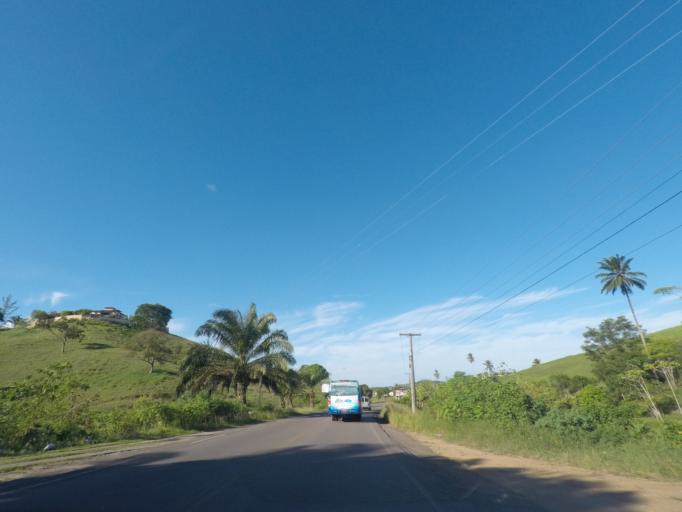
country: BR
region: Bahia
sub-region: Nazare
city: Nazare
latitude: -13.0454
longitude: -39.0064
